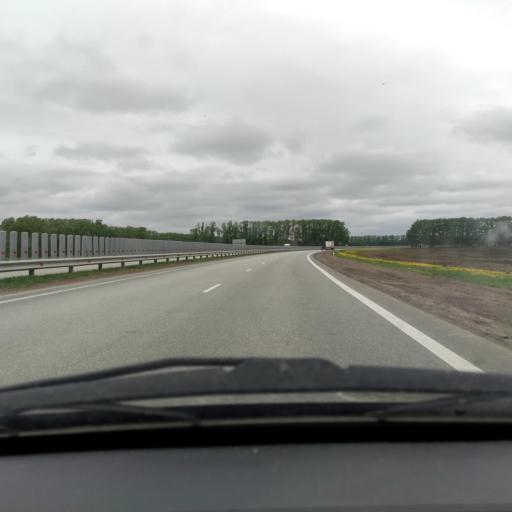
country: RU
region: Bashkortostan
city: Asanovo
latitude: 54.9225
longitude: 55.5801
